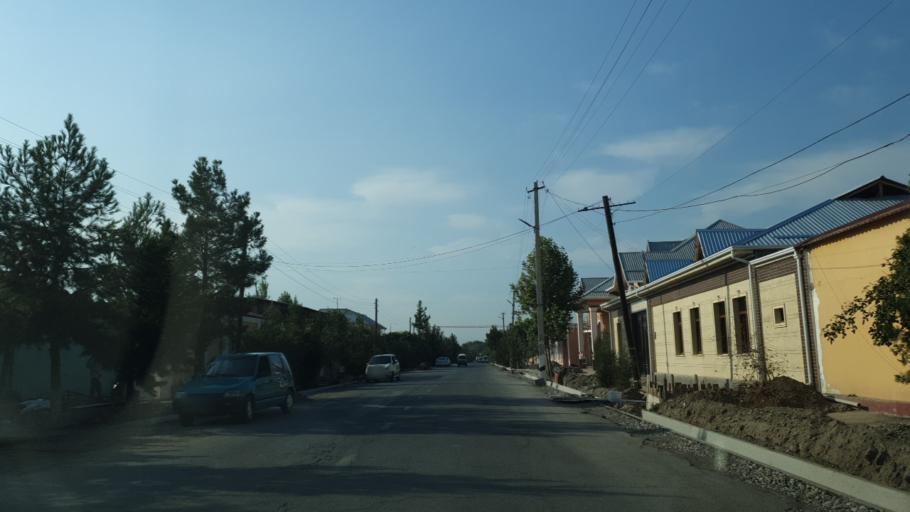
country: UZ
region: Fergana
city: Yaypan
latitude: 40.3708
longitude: 70.8135
